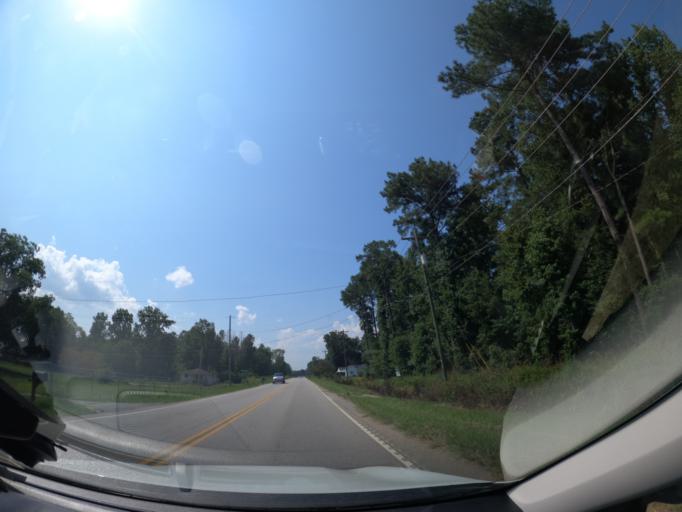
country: US
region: South Carolina
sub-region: Richland County
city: Hopkins
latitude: 33.9290
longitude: -80.9658
